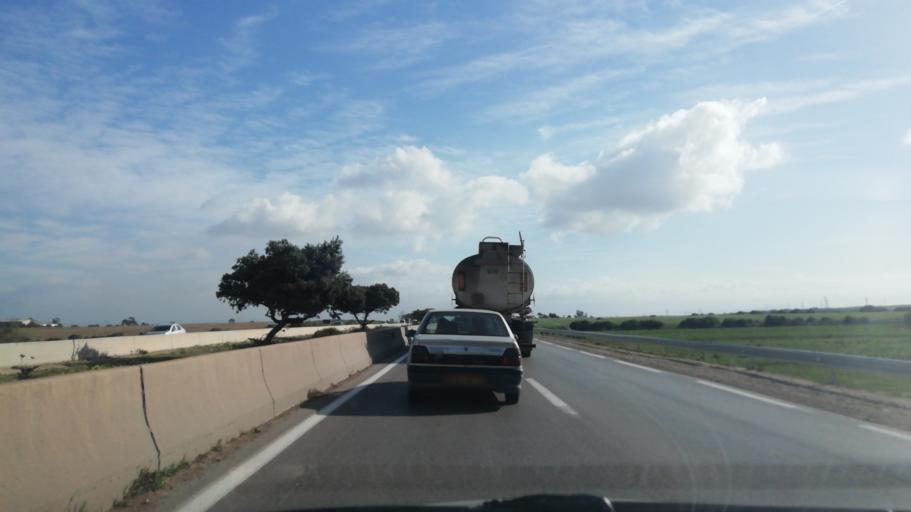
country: DZ
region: Oran
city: Ain el Bya
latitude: 35.7670
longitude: -0.2182
